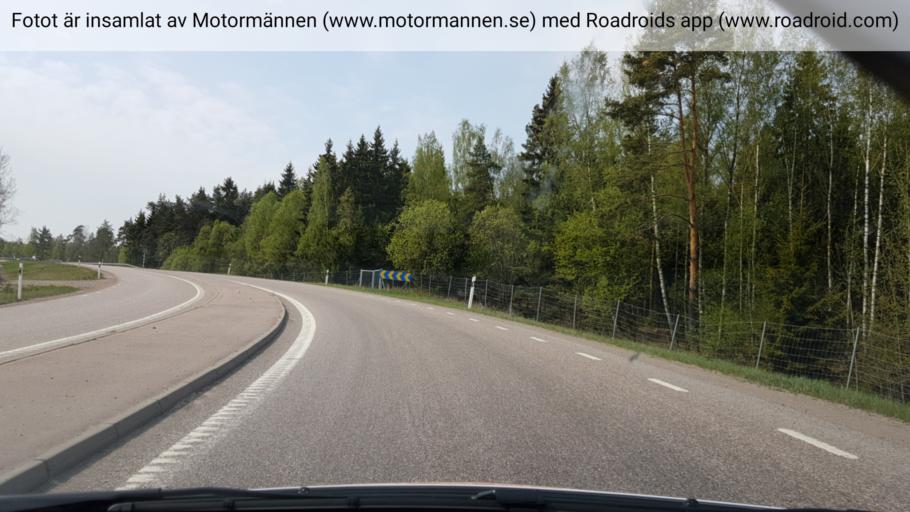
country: SE
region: Vaestmanland
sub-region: Hallstahammars Kommun
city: Kolback
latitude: 59.5823
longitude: 16.3540
